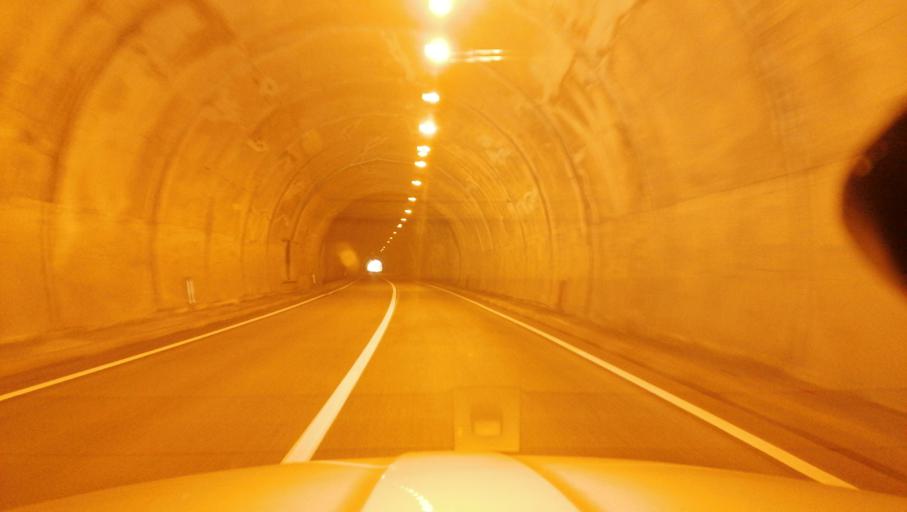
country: BA
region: Republika Srpska
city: Visegrad
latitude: 43.7396
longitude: 19.2112
